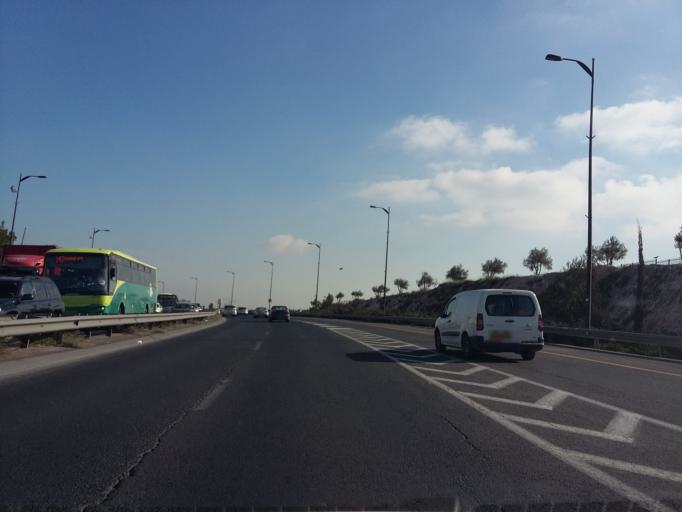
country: PS
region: West Bank
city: `Anata
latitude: 31.8101
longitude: 35.2375
